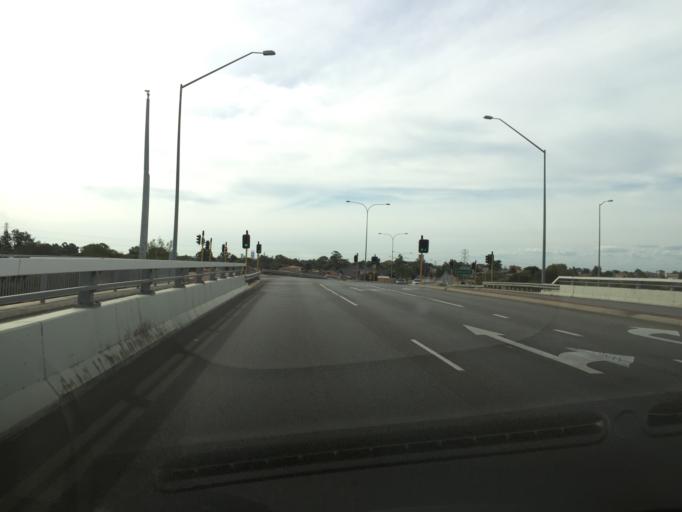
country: AU
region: Western Australia
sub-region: Canning
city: Canning Vale
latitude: -32.0572
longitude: 115.9048
